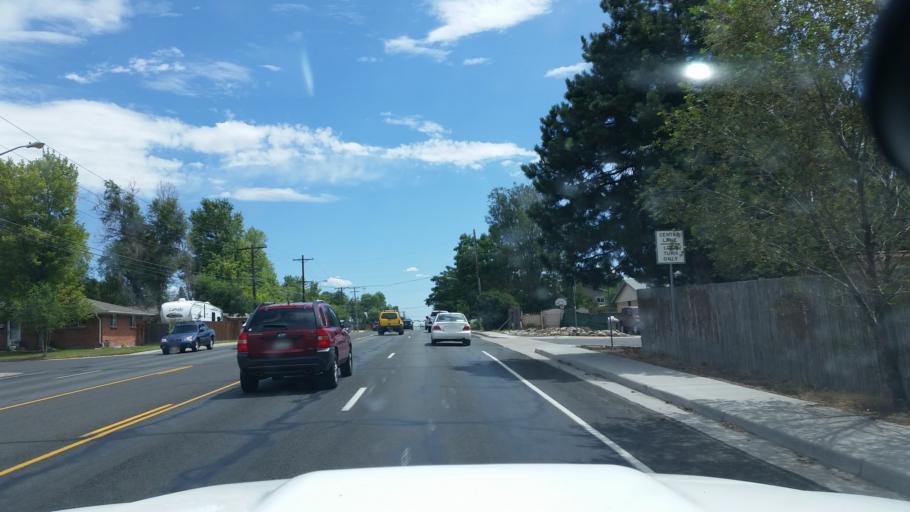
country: US
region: Colorado
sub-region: Adams County
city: Westminster
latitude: 39.8634
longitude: -105.0330
